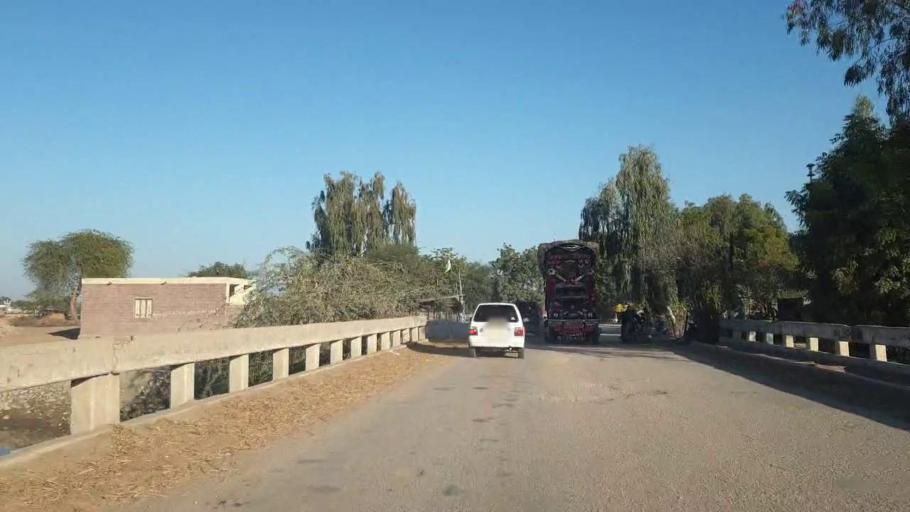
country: PK
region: Sindh
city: Dokri
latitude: 27.3652
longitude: 68.1147
